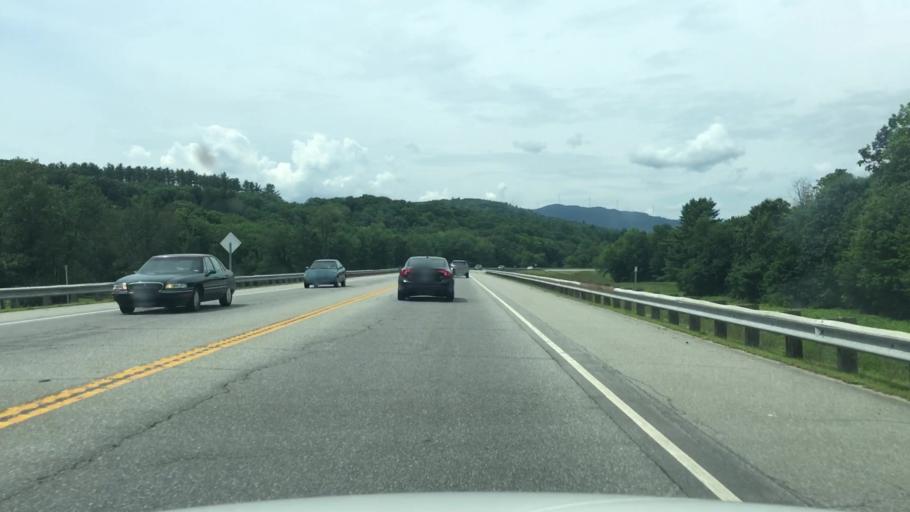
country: US
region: New Hampshire
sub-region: Grafton County
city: Plymouth
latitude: 43.7686
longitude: -71.6951
